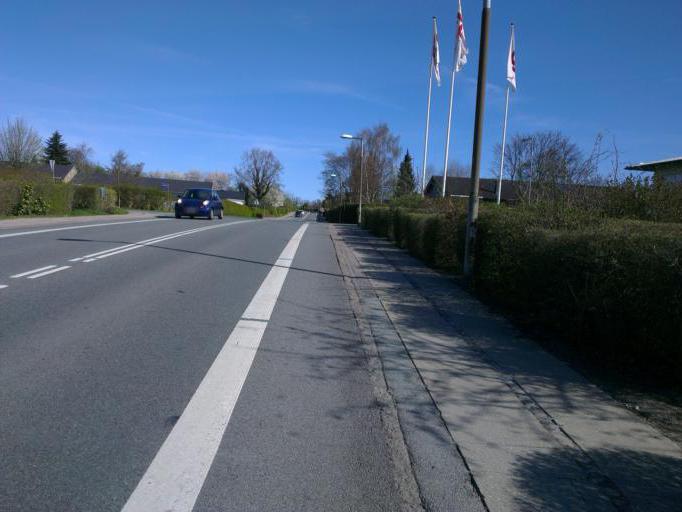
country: DK
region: Capital Region
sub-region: Frederikssund Kommune
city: Frederikssund
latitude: 55.8382
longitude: 12.0746
